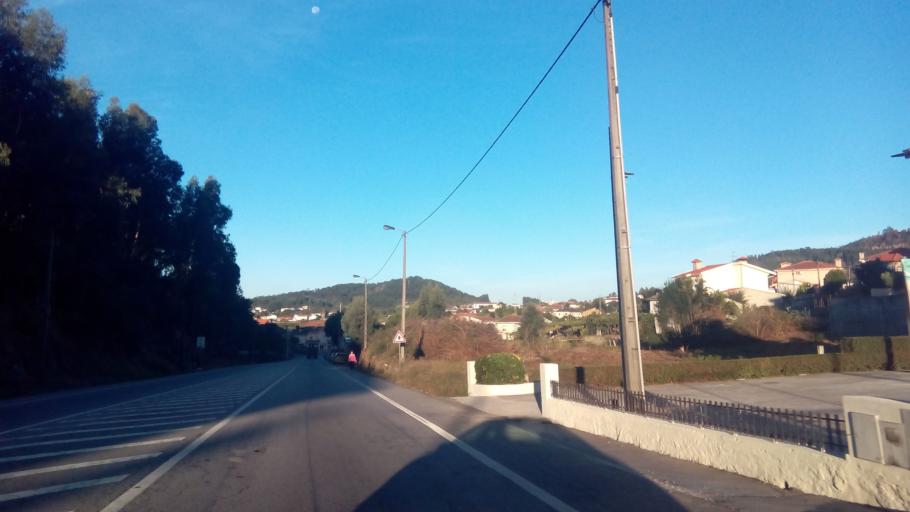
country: PT
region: Porto
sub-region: Paredes
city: Baltar
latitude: 41.1871
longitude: -8.3732
